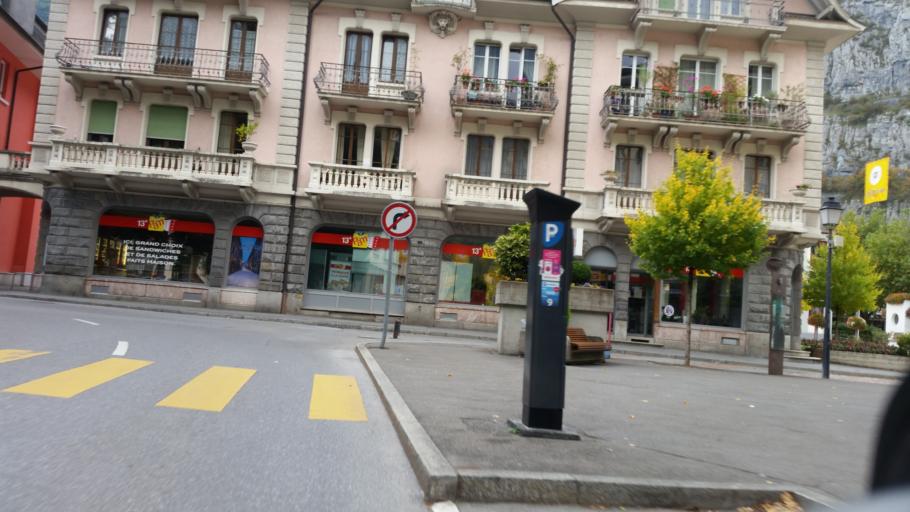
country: CH
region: Valais
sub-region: Saint-Maurice District
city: Saint-Maurice
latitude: 46.2176
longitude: 7.0048
